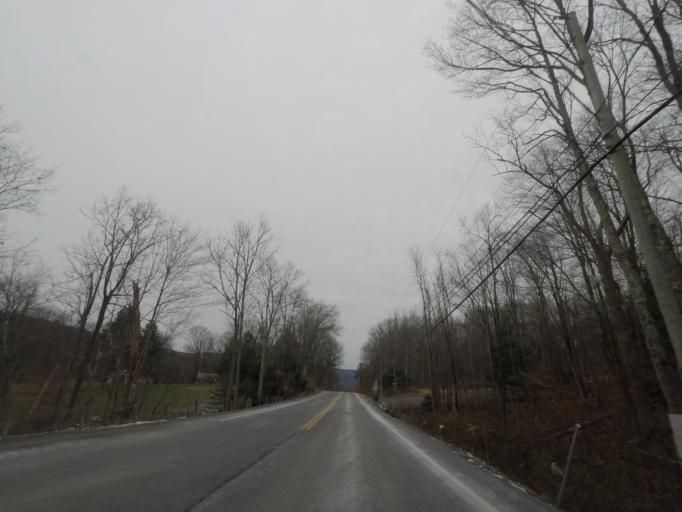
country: US
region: New York
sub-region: Rensselaer County
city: Hoosick Falls
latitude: 42.7561
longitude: -73.3615
